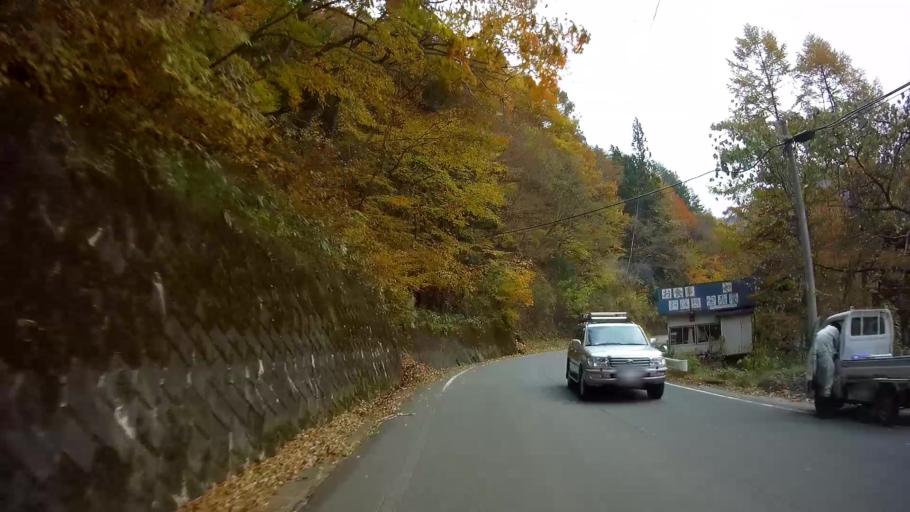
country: JP
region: Gunma
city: Nakanojomachi
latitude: 36.6473
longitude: 138.6507
